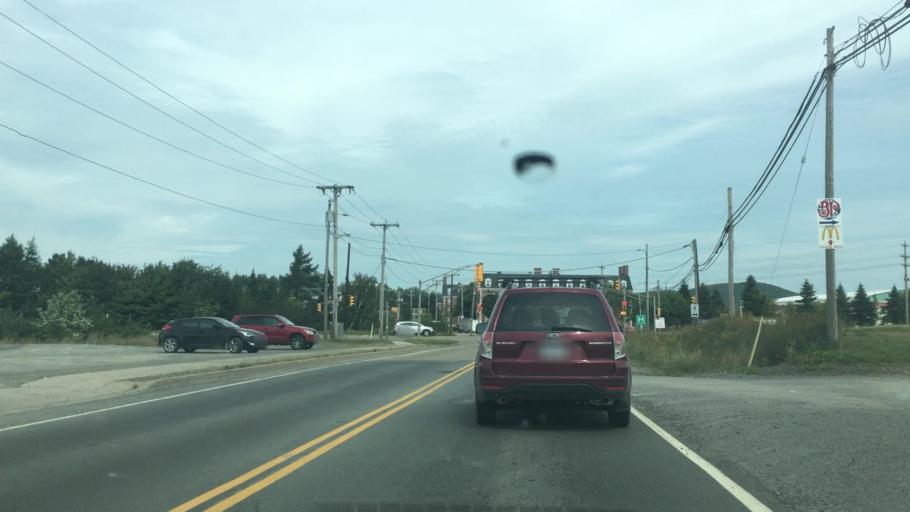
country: CA
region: Nova Scotia
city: Antigonish
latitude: 45.6133
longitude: -61.9988
